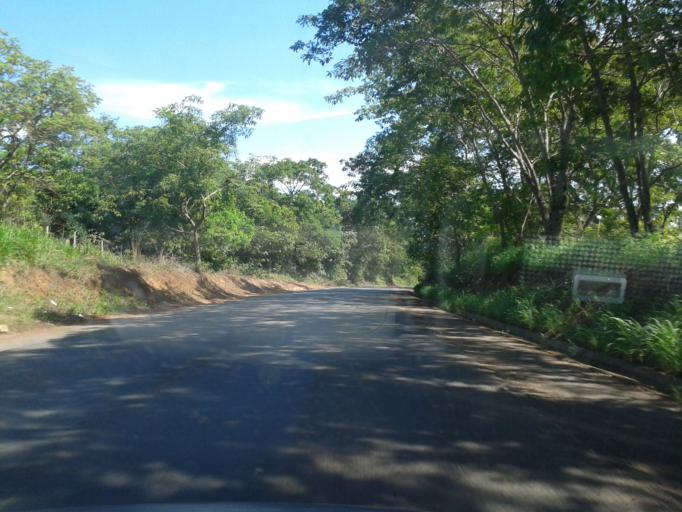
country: BR
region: Goias
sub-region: Piracanjuba
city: Piracanjuba
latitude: -17.2260
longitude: -48.7135
